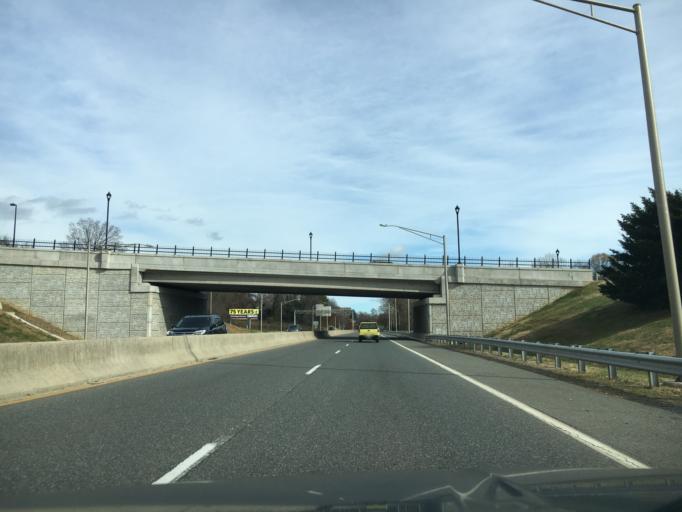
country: US
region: Virginia
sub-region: City of Lynchburg
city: Lynchburg
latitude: 37.3991
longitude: -79.1515
